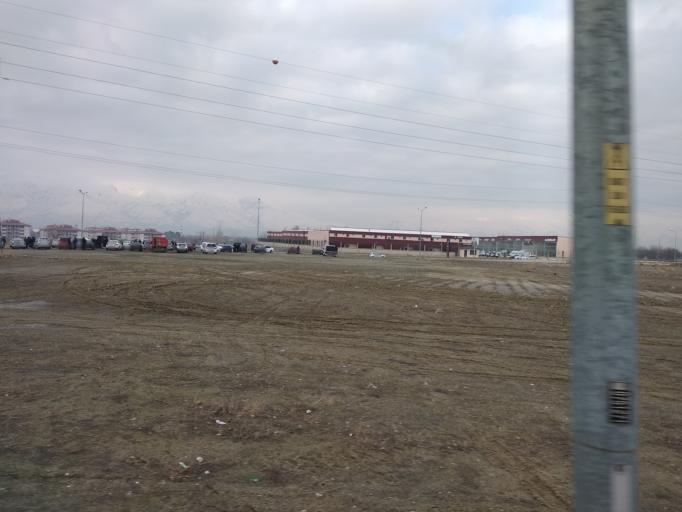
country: TR
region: Erzincan
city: Erzincan
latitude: 39.7316
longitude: 39.5337
